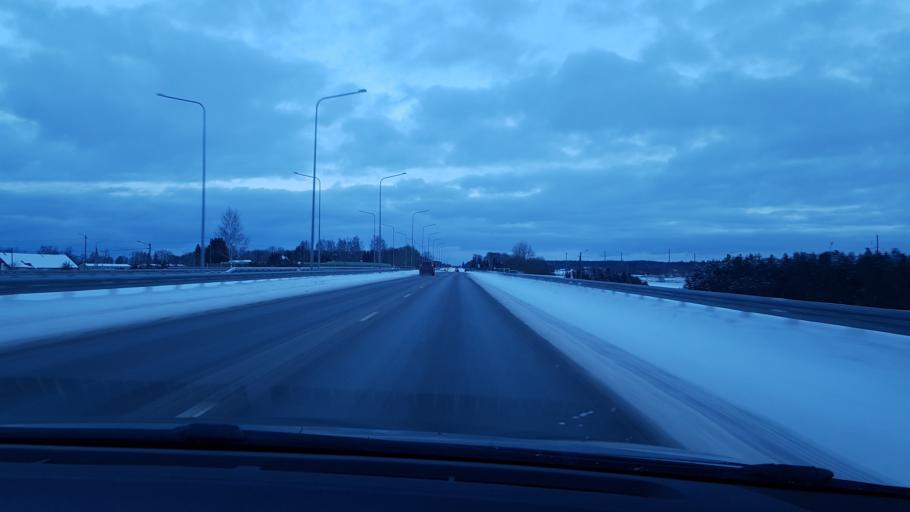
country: EE
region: Harju
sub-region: Kuusalu vald
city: Kuusalu
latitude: 59.4450
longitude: 25.3743
